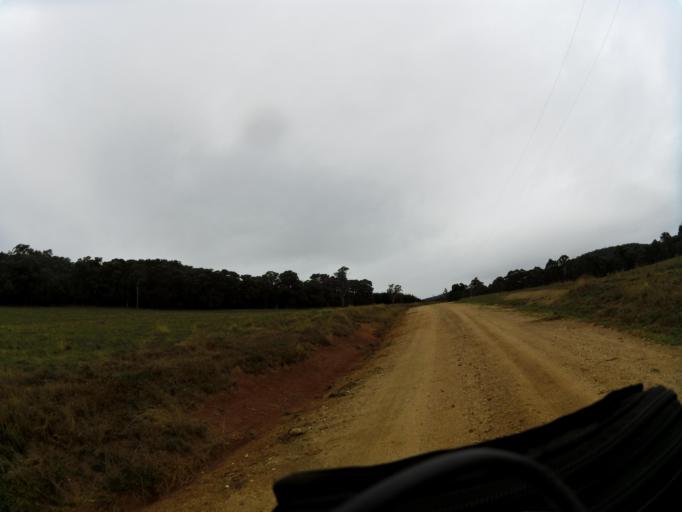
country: AU
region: New South Wales
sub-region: Greater Hume Shire
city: Holbrook
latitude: -36.1652
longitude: 147.4953
